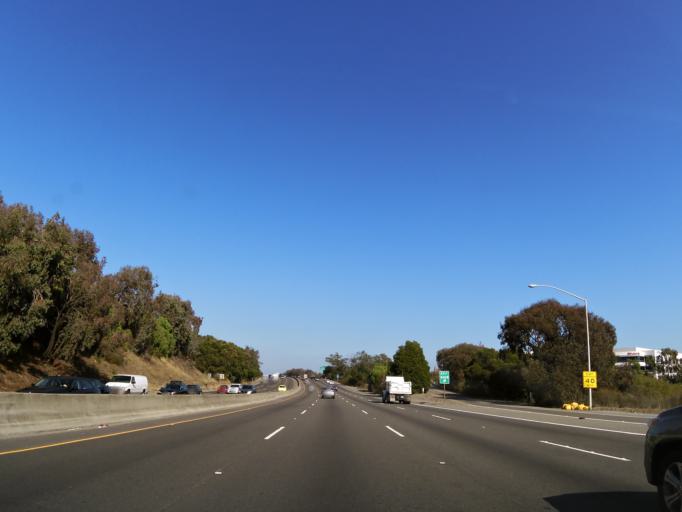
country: US
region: California
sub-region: San Mateo County
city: Brisbane
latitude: 37.6704
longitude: -122.3921
